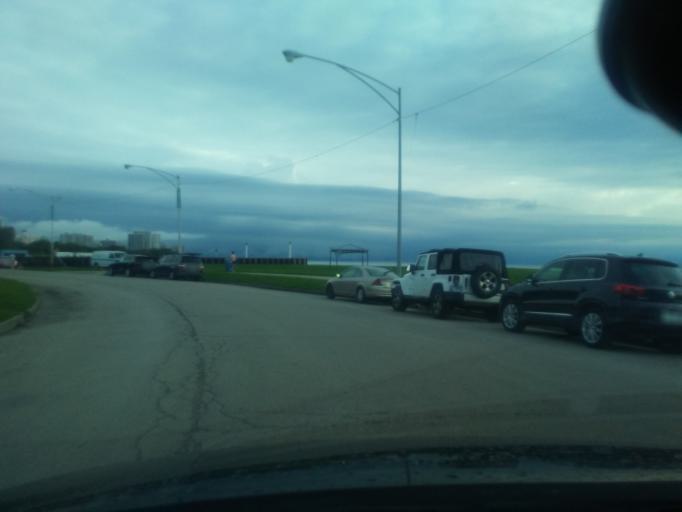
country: US
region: Illinois
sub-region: Cook County
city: Evanston
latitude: 41.9674
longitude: -87.6425
